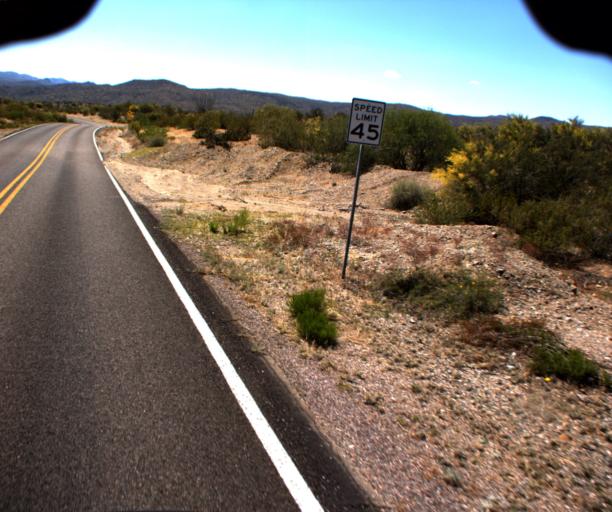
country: US
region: Arizona
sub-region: Yavapai County
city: Bagdad
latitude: 34.4800
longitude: -113.2018
